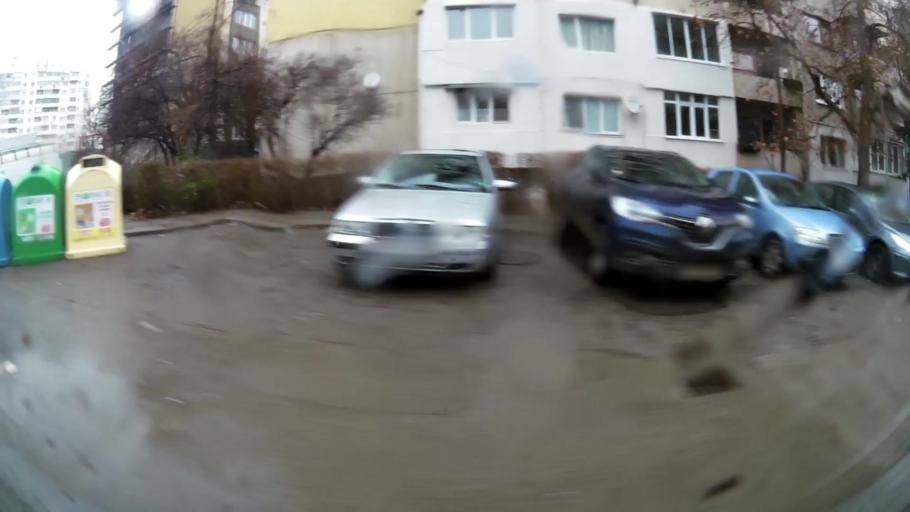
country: BG
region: Sofia-Capital
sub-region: Stolichna Obshtina
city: Sofia
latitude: 42.6530
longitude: 23.3626
